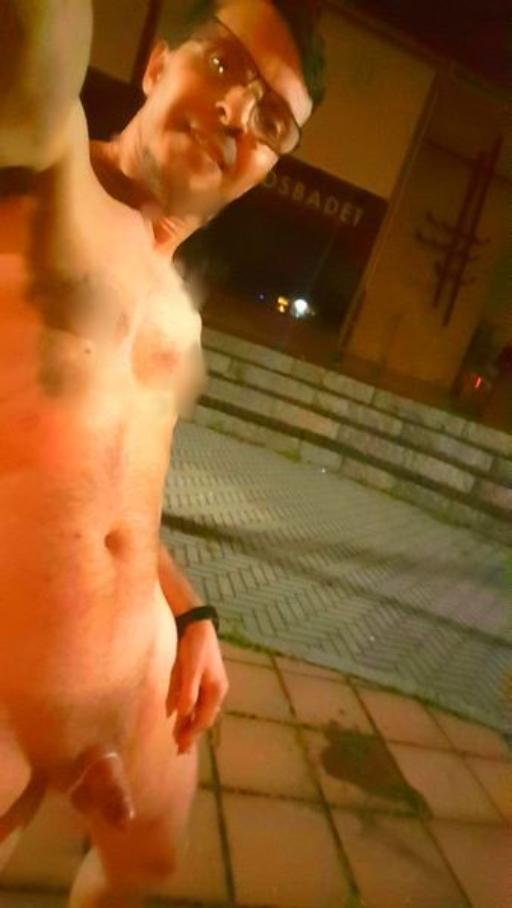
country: SE
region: Gaevleborg
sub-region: Hudiksvalls Kommun
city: Iggesund
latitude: 61.6427
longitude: 17.0764
